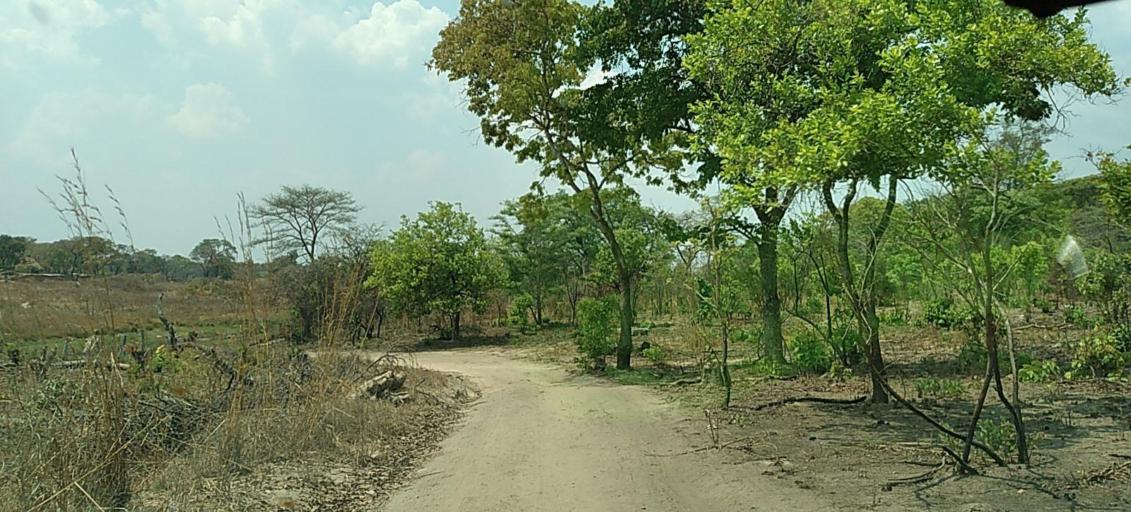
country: ZM
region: North-Western
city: Kabompo
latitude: -13.6350
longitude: 24.3851
